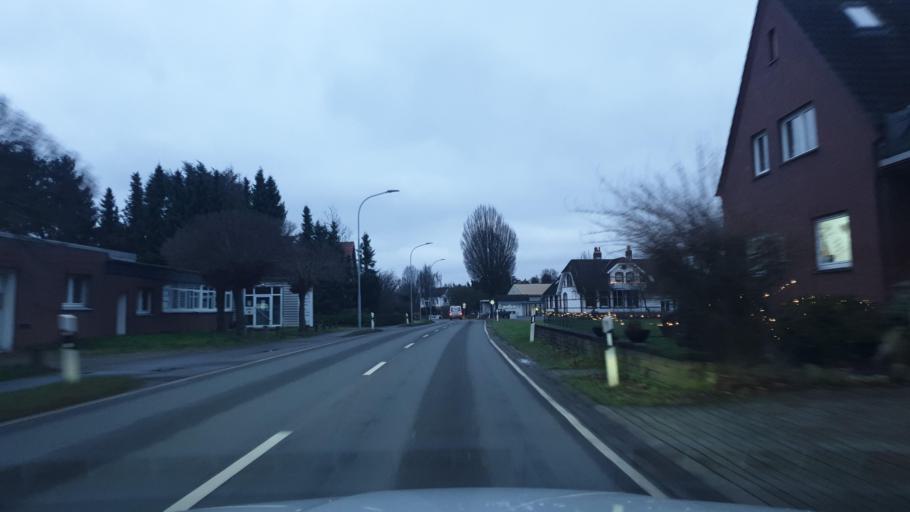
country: DE
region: North Rhine-Westphalia
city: Bad Oeynhausen
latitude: 52.1754
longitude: 8.8116
